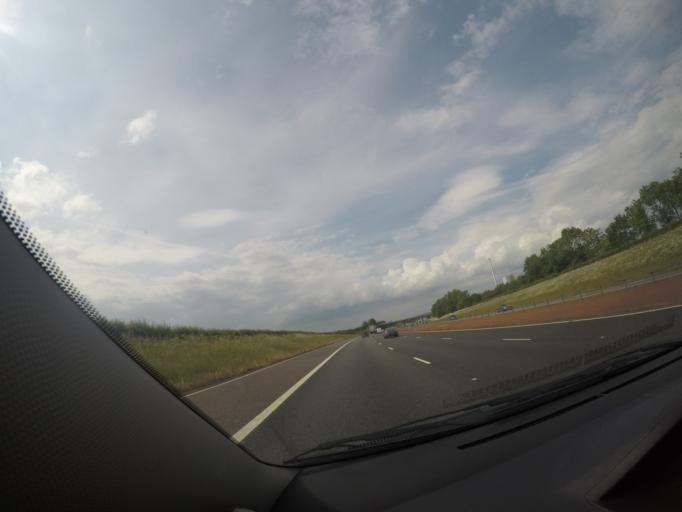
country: GB
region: Scotland
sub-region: Dumfries and Galloway
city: Lockerbie
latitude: 55.1473
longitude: -3.3811
